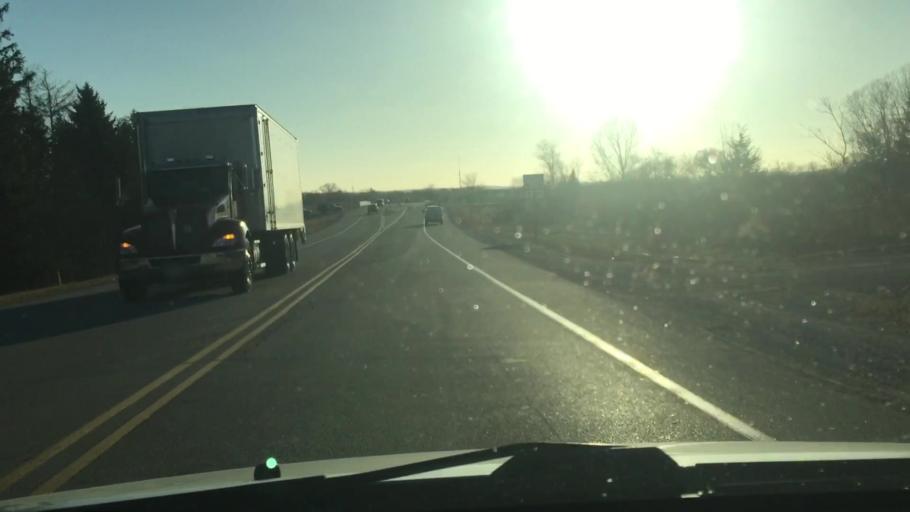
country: US
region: Wisconsin
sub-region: Waukesha County
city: Pewaukee
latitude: 43.0974
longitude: -88.2703
